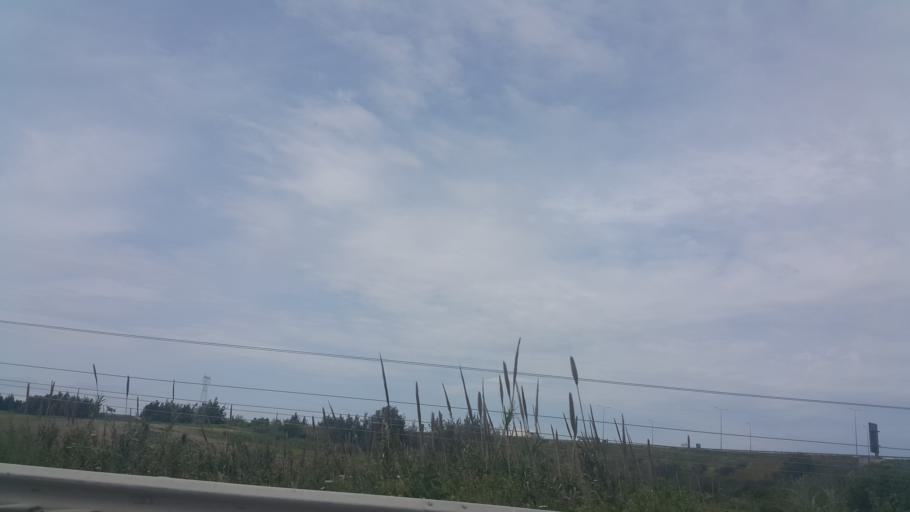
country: TR
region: Adana
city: Yakapinar
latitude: 37.0038
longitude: 35.6926
